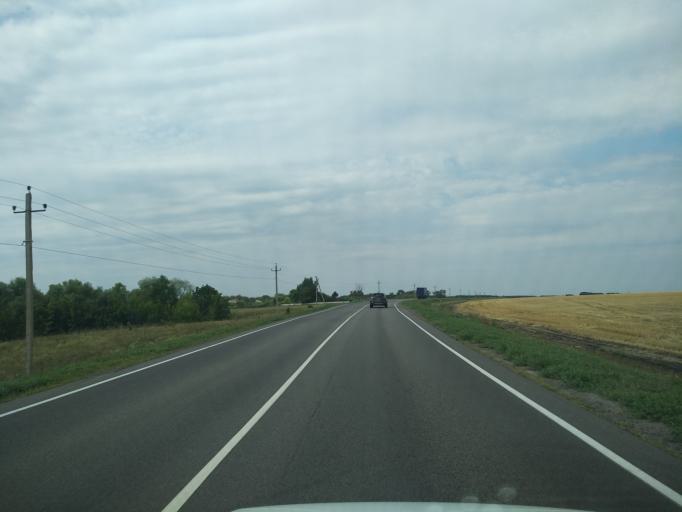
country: RU
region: Voronezj
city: Pereleshinskiy
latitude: 51.8163
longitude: 40.2602
